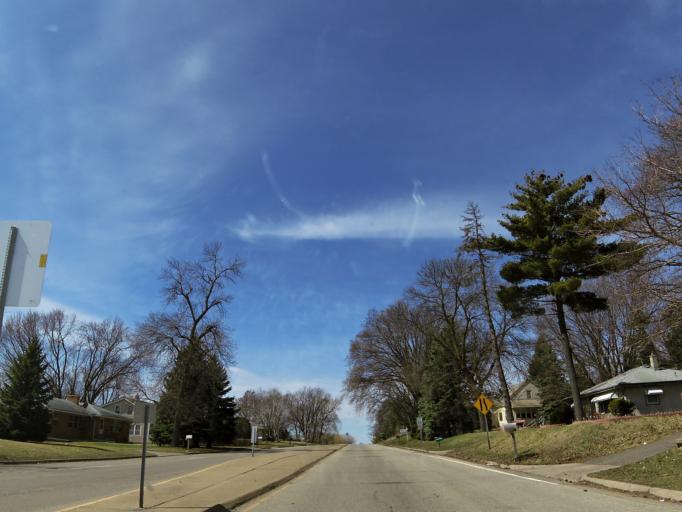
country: US
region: Minnesota
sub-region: Ramsey County
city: North Saint Paul
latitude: 44.9921
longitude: -93.0259
